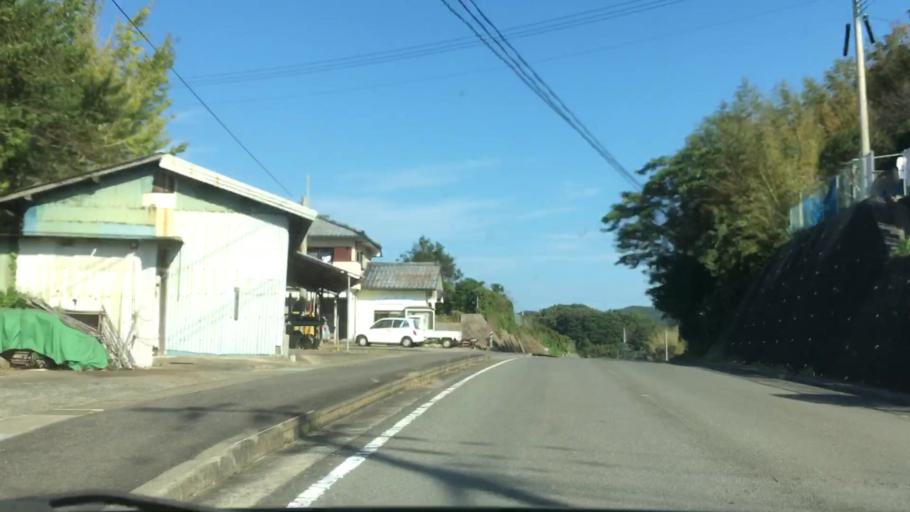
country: JP
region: Nagasaki
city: Sasebo
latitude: 33.0157
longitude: 129.6543
